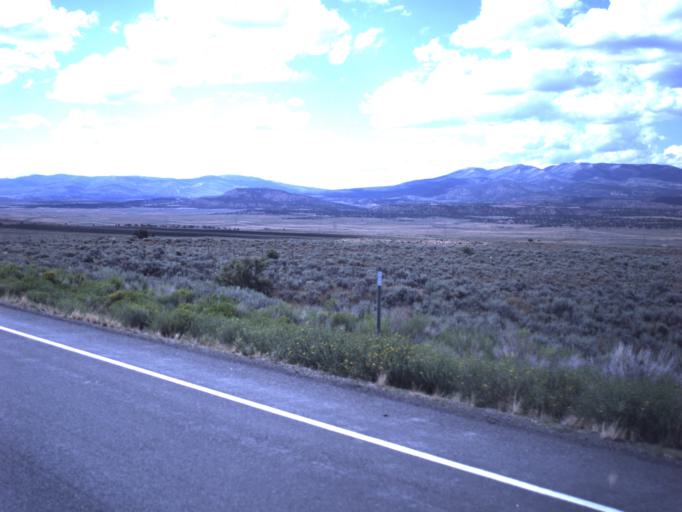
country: US
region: Utah
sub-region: Duchesne County
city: Duchesne
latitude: 40.2037
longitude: -110.7181
